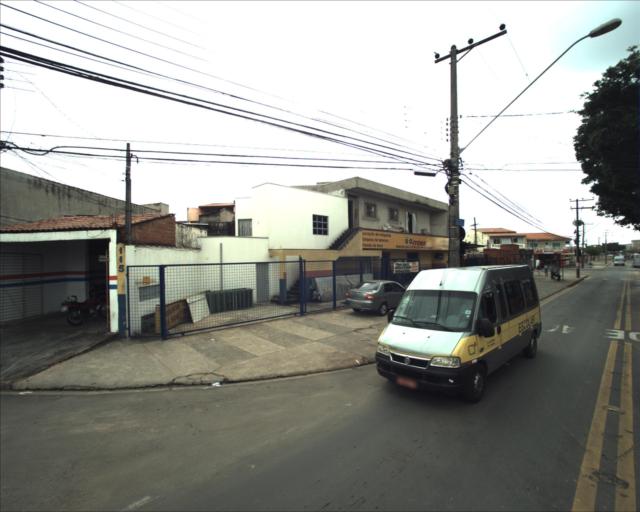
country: BR
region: Sao Paulo
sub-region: Sorocaba
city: Sorocaba
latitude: -23.4326
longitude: -47.4674
